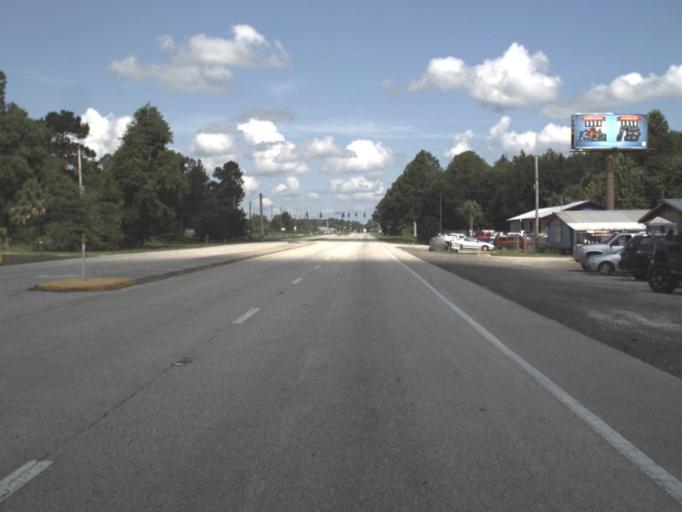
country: US
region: Florida
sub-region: Putnam County
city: Palatka
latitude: 29.6610
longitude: -81.6765
